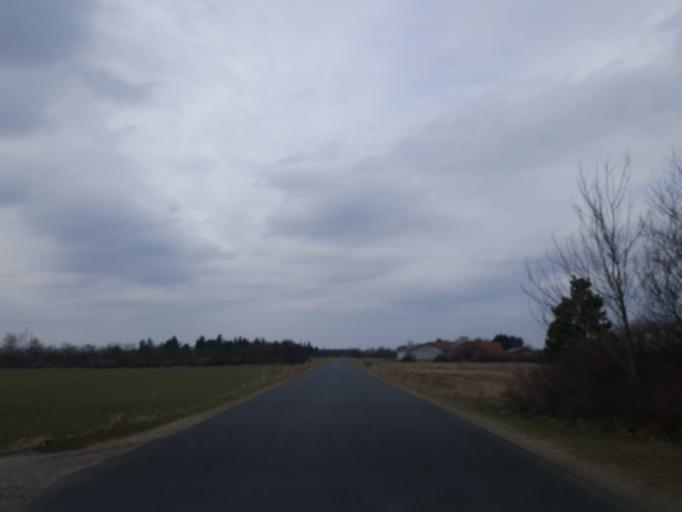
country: DK
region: Central Jutland
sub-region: Holstebro Kommune
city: Ulfborg
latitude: 56.3515
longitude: 8.2840
